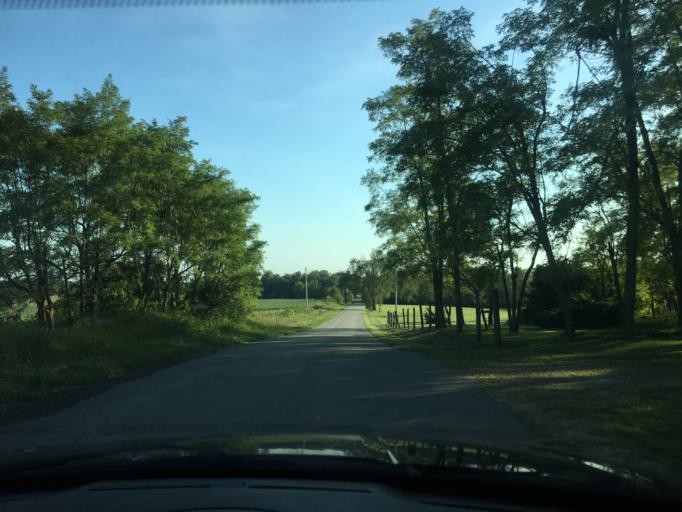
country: US
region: Ohio
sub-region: Logan County
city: West Liberty
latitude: 40.2466
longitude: -83.6664
